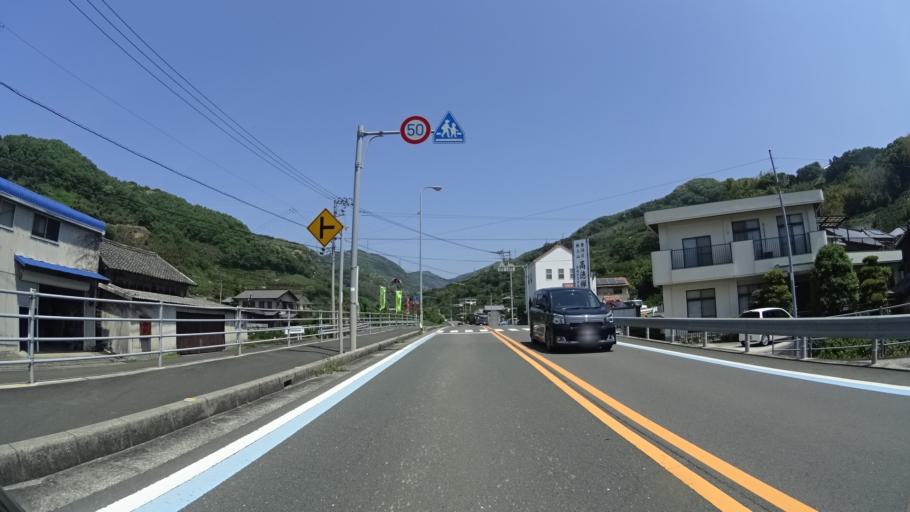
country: JP
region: Ehime
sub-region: Nishiuwa-gun
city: Ikata-cho
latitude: 33.4951
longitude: 132.3971
